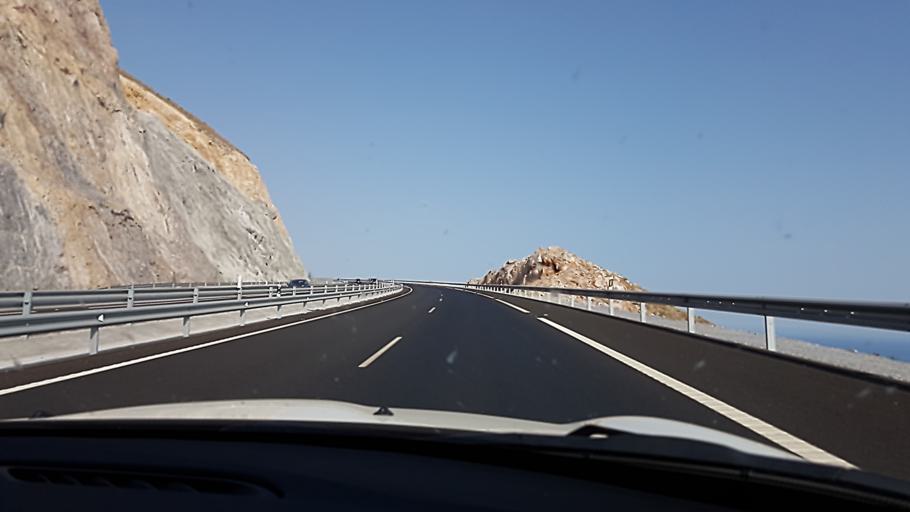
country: ES
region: Andalusia
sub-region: Provincia de Granada
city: Gualchos
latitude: 36.7151
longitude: -3.3892
